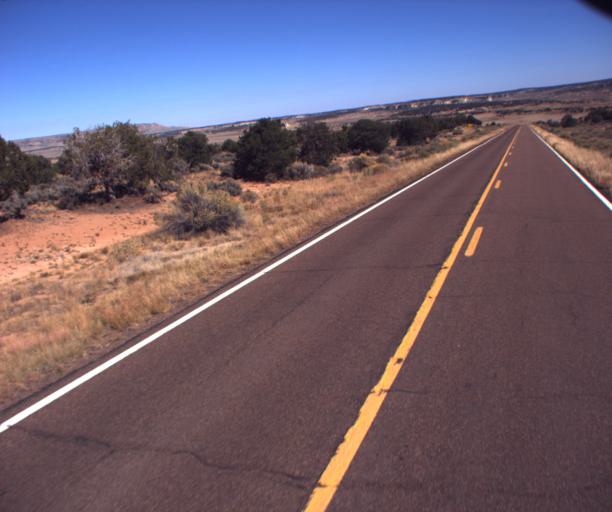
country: US
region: Arizona
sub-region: Apache County
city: Ganado
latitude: 35.7524
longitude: -109.9040
